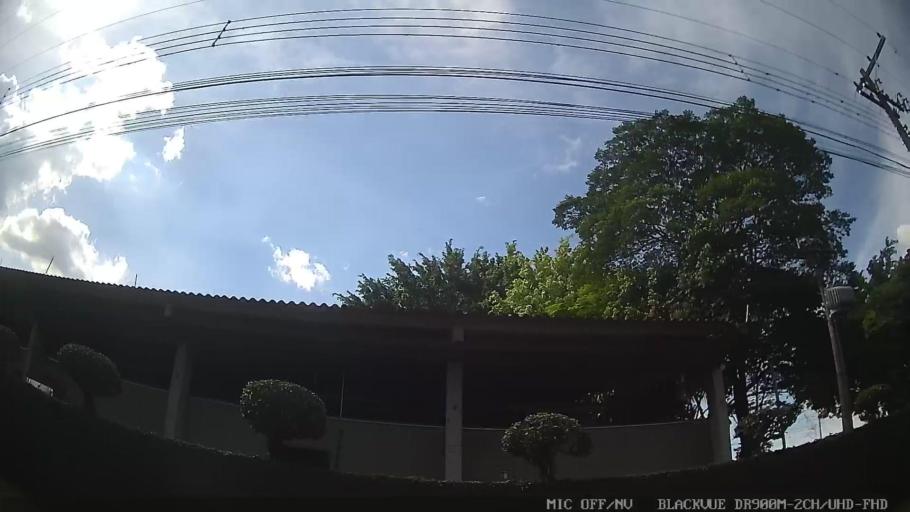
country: BR
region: Sao Paulo
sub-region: Jaguariuna
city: Jaguariuna
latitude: -22.6275
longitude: -47.0560
